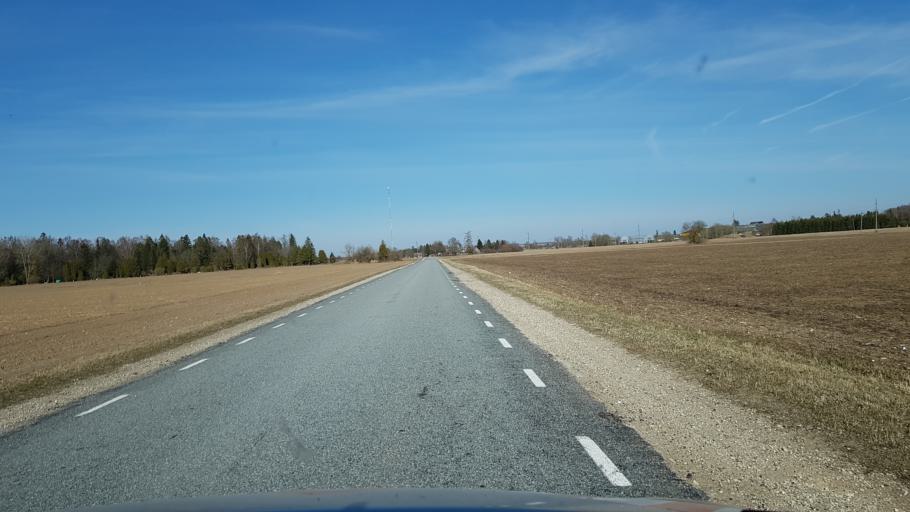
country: EE
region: Laeaene-Virumaa
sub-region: Rakke vald
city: Rakke
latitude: 59.0450
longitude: 26.3699
